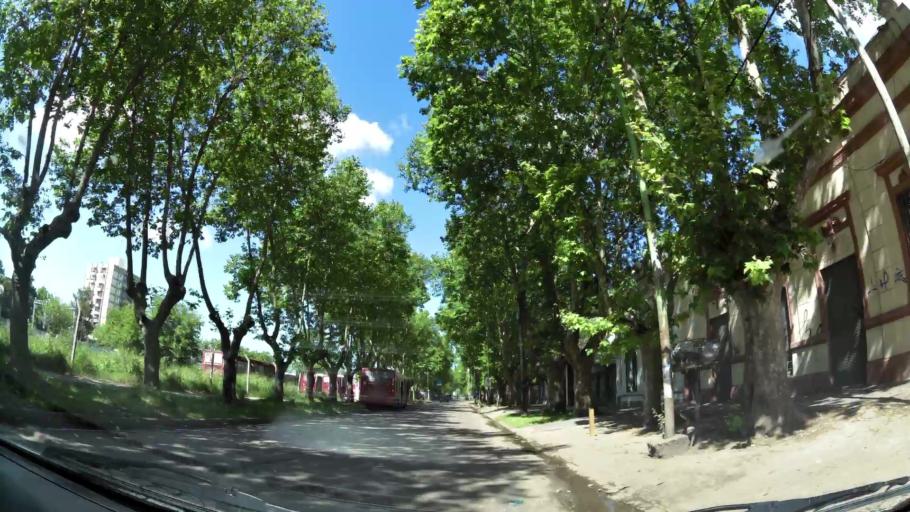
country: AR
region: Buenos Aires
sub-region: Partido de Quilmes
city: Quilmes
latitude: -34.8118
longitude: -58.2756
